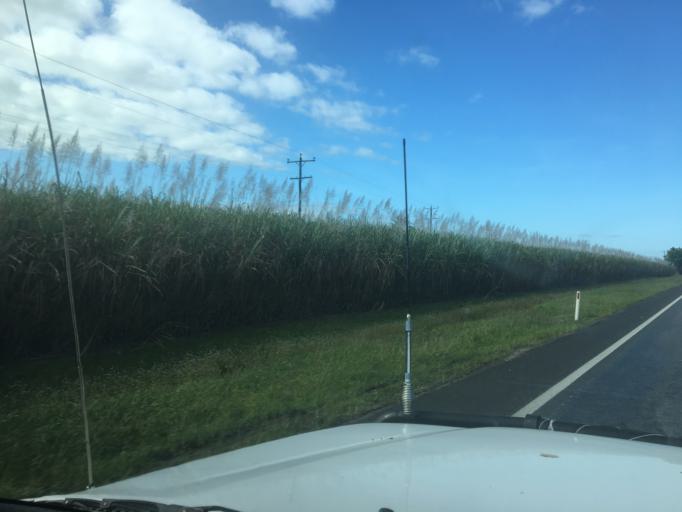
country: AU
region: Queensland
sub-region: Cassowary Coast
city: Innisfail
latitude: -17.3011
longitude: 145.9279
